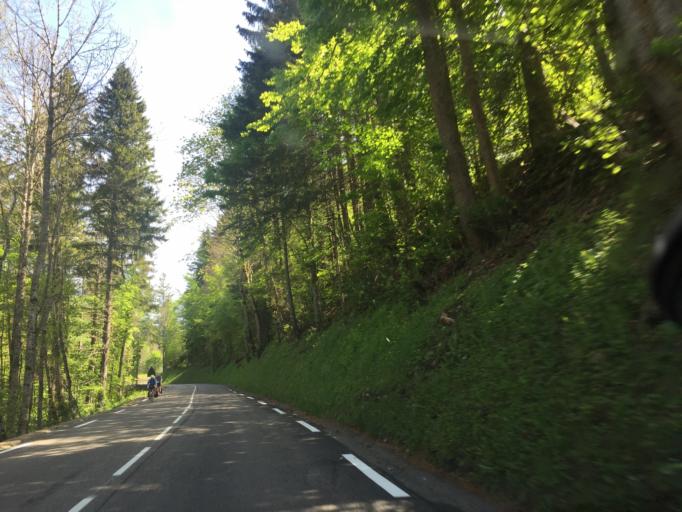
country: FR
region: Rhone-Alpes
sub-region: Departement de l'Isere
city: Saint-Hilaire
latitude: 45.3548
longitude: 5.8240
